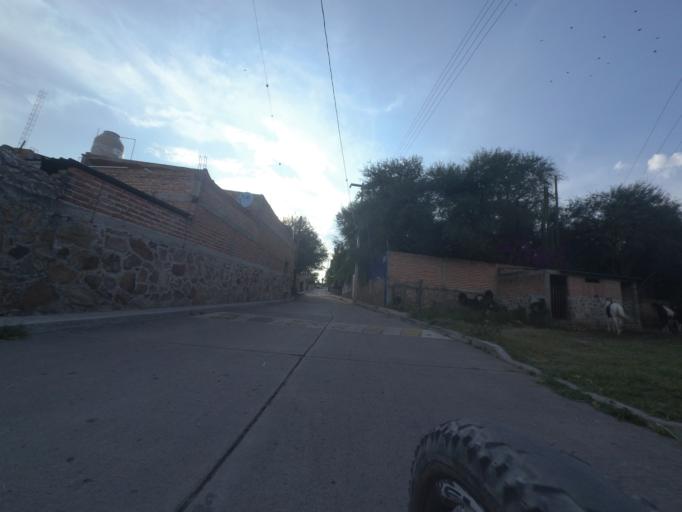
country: MX
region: Aguascalientes
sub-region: Aguascalientes
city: Los Canos
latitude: 21.7800
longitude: -102.3740
